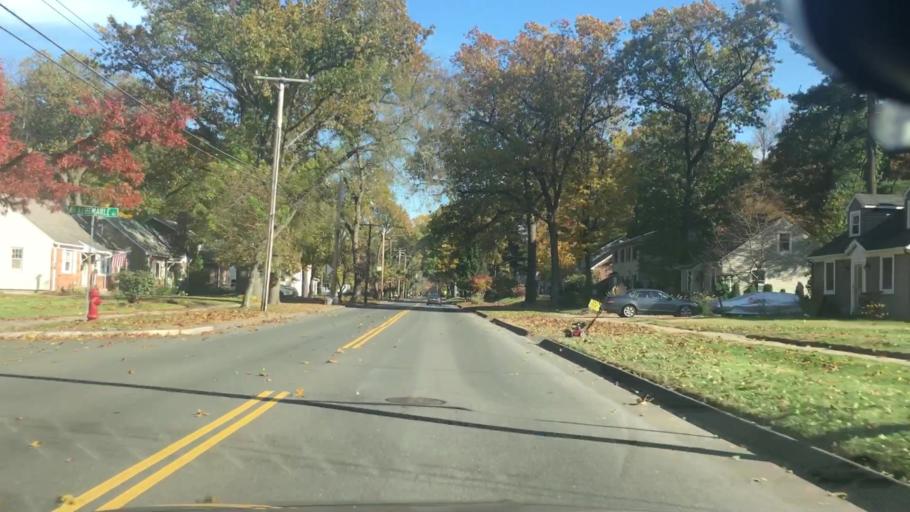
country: US
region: Connecticut
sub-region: Hartford County
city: Sherwood Manor
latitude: 42.0318
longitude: -72.5690
